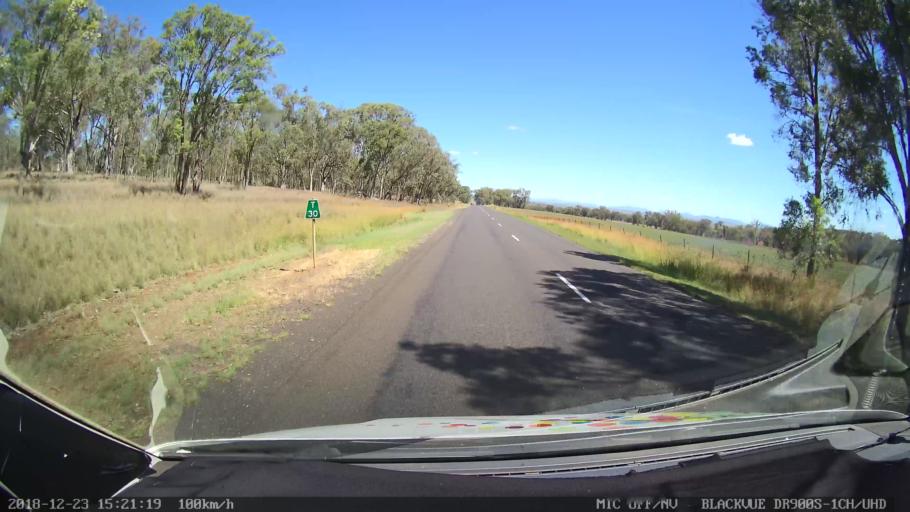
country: AU
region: New South Wales
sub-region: Tamworth Municipality
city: Manilla
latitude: -30.8548
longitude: 150.7958
